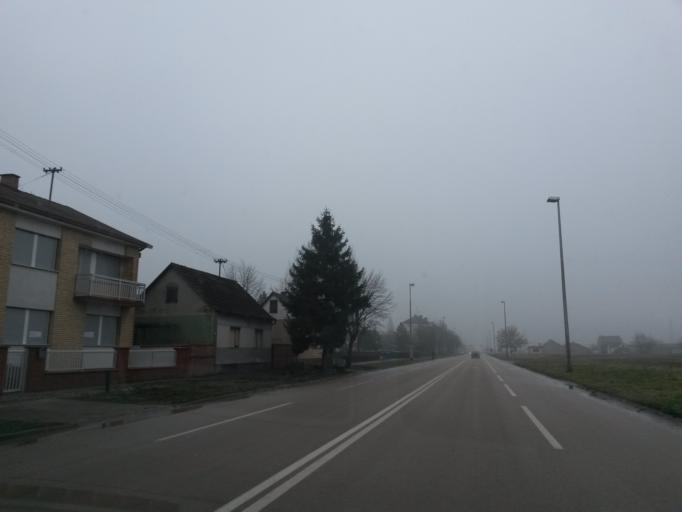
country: HR
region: Vukovarsko-Srijemska
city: Zupanja
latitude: 45.0844
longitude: 18.6961
